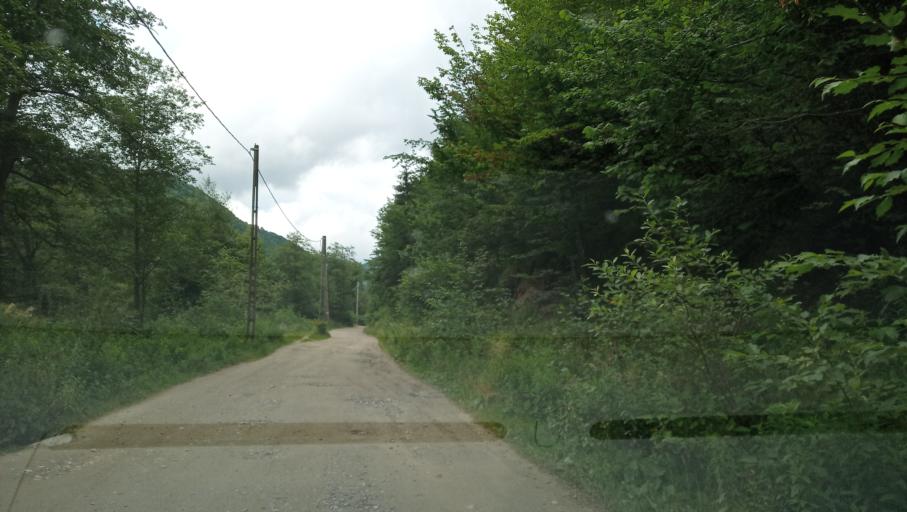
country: RO
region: Hunedoara
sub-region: Oras Petrila
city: Petrila
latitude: 45.4806
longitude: 23.4164
